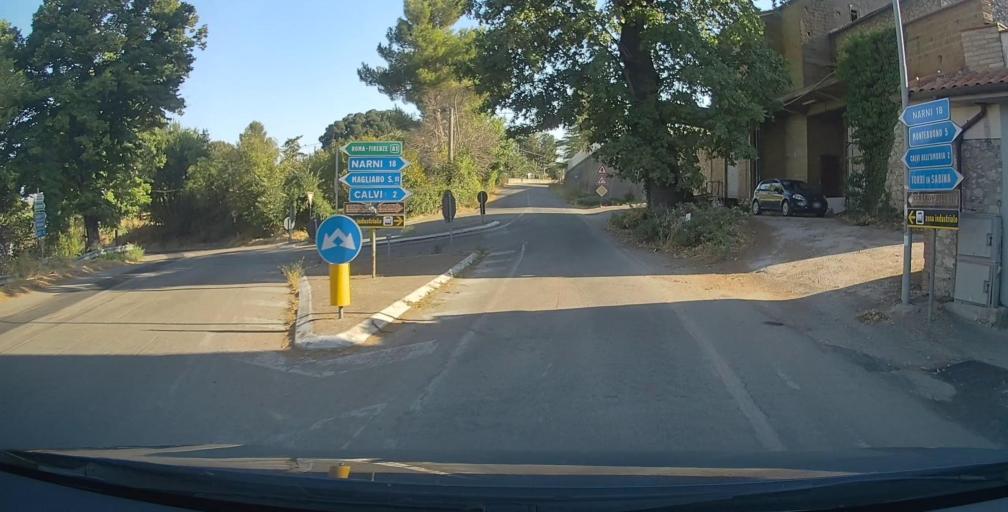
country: IT
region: Umbria
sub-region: Provincia di Terni
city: Calvi dell'Umbria
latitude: 42.3935
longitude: 12.5649
